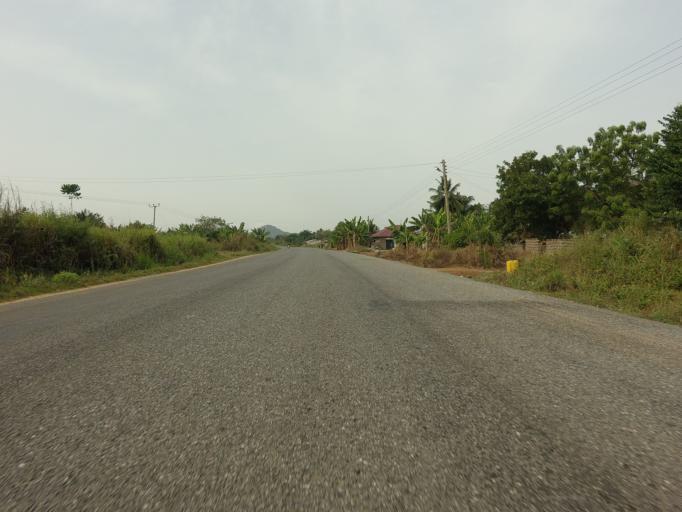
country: GH
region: Volta
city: Ho
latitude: 6.4192
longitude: 0.1796
